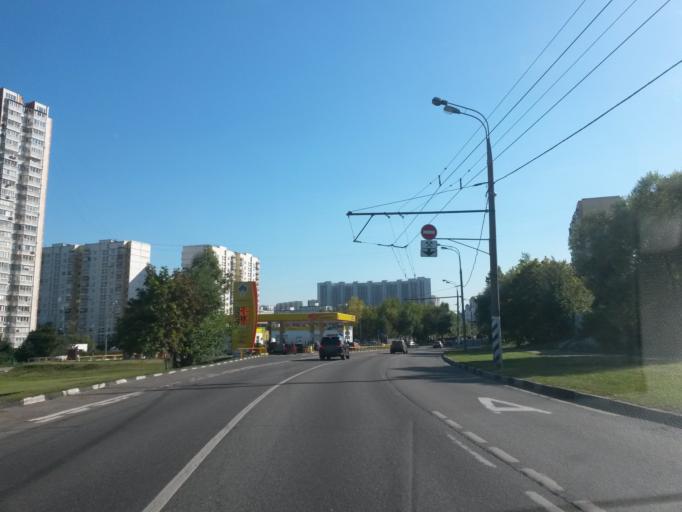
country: RU
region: Moscow
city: Yasenevo
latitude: 55.6210
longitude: 37.5426
